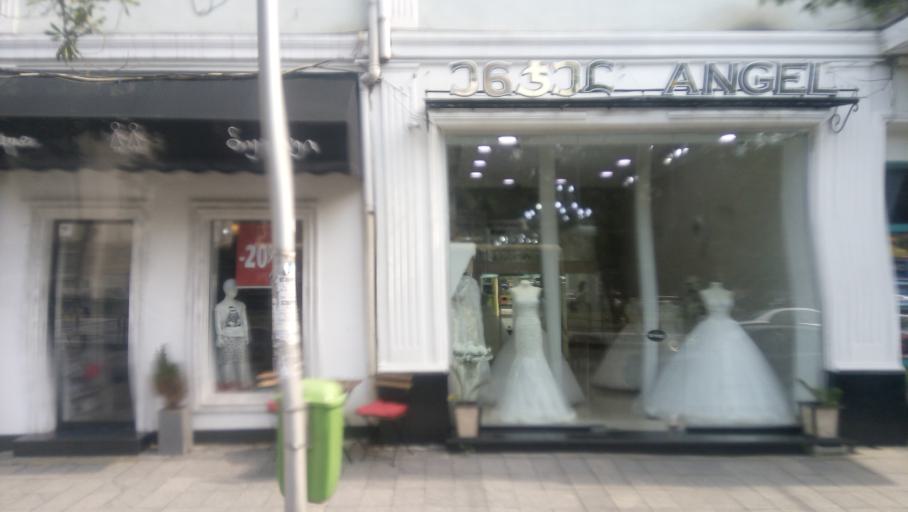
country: GE
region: Ajaria
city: Batumi
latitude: 41.6484
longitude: 41.6337
